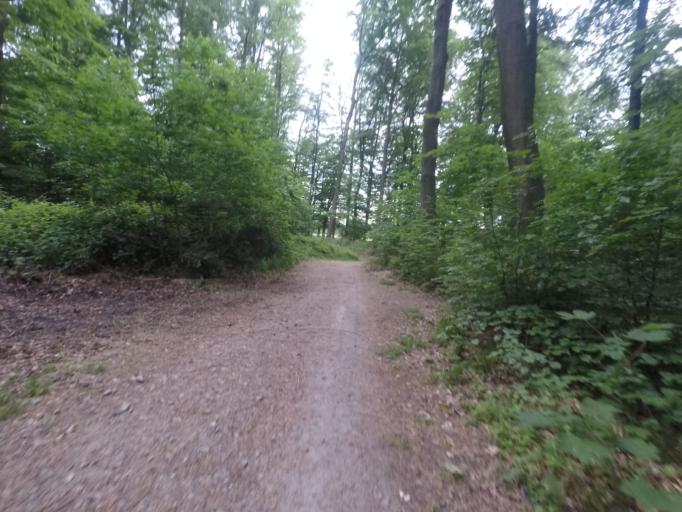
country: DE
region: North Rhine-Westphalia
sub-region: Regierungsbezirk Detmold
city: Bad Salzuflen
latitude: 52.1037
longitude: 8.7258
